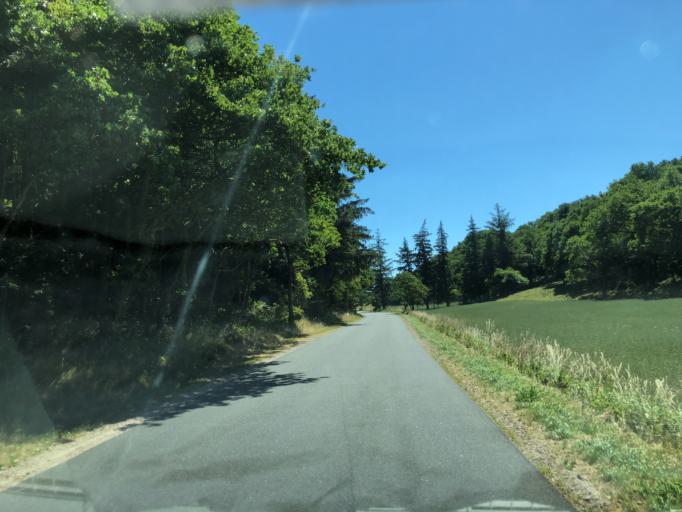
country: DK
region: Central Jutland
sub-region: Viborg Kommune
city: Viborg
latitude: 56.5428
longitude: 9.4571
